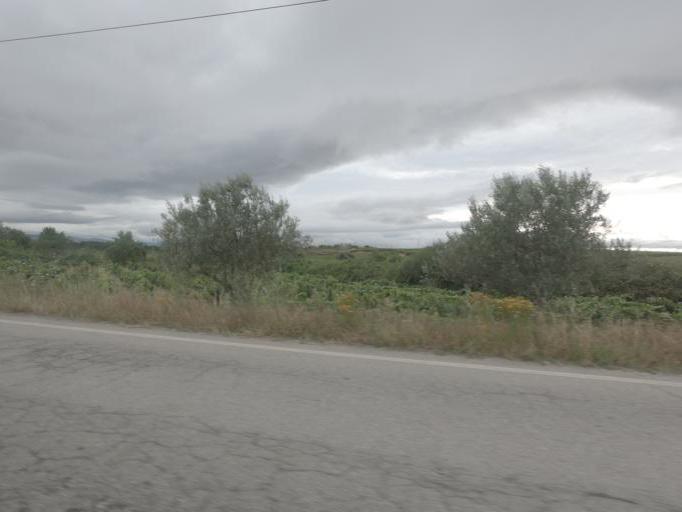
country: PT
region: Vila Real
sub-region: Sabrosa
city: Sabrosa
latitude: 41.2782
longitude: -7.5107
